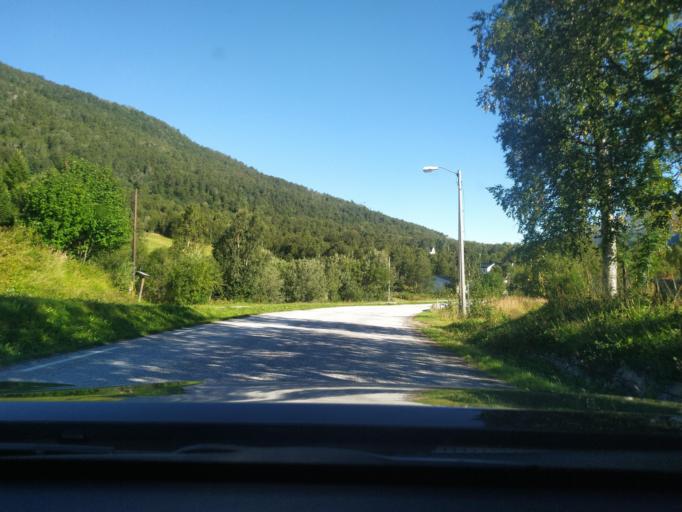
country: NO
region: Troms
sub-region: Salangen
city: Sjovegan
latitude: 68.9365
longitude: 17.7166
